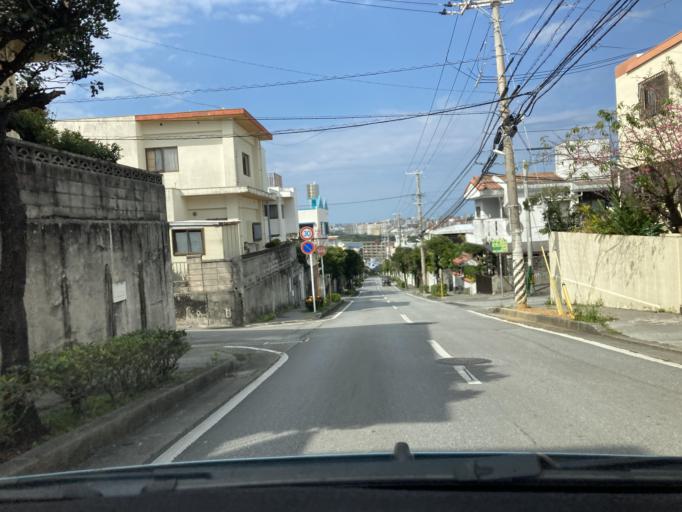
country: JP
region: Okinawa
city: Tomigusuku
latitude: 26.1876
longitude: 127.6956
